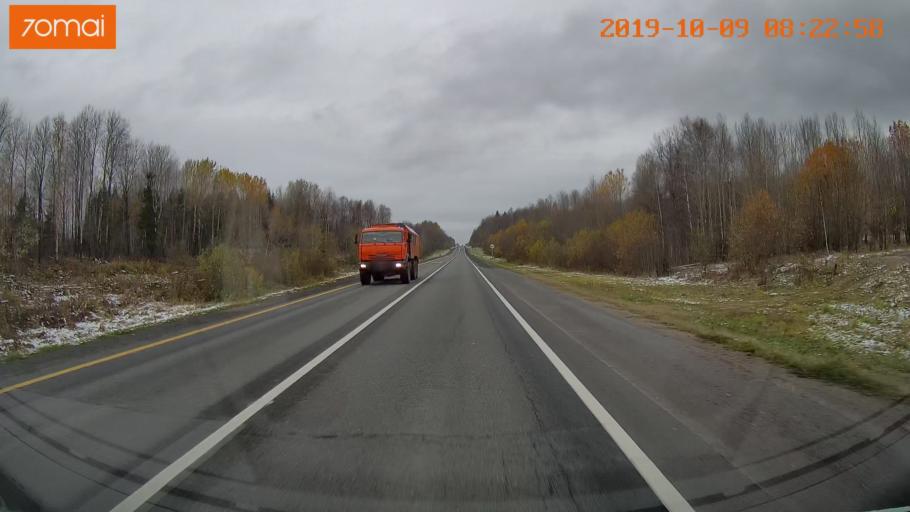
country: RU
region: Vologda
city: Gryazovets
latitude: 58.7484
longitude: 40.2859
